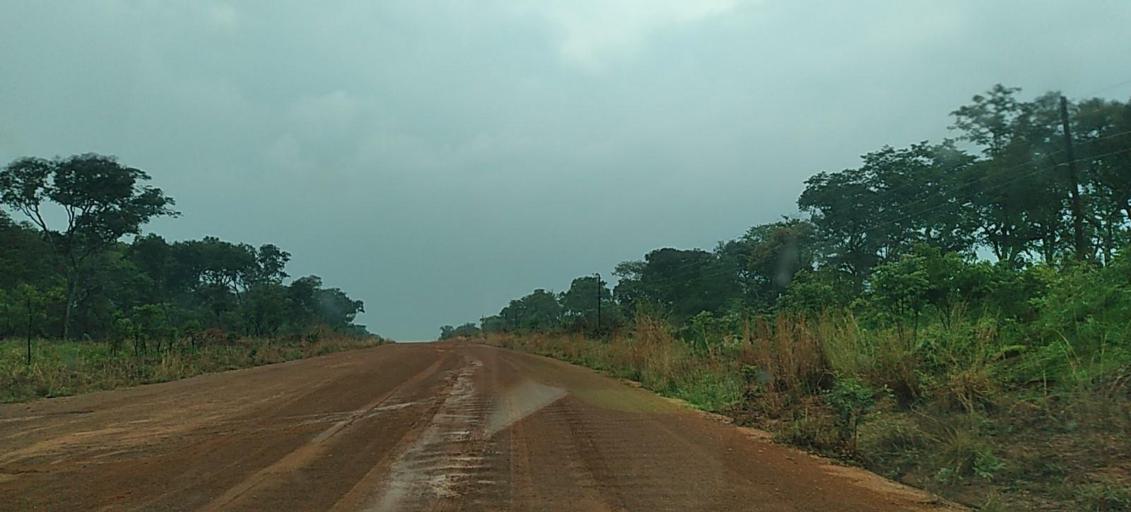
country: ZM
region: North-Western
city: Mwinilunga
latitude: -11.6048
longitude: 24.3952
